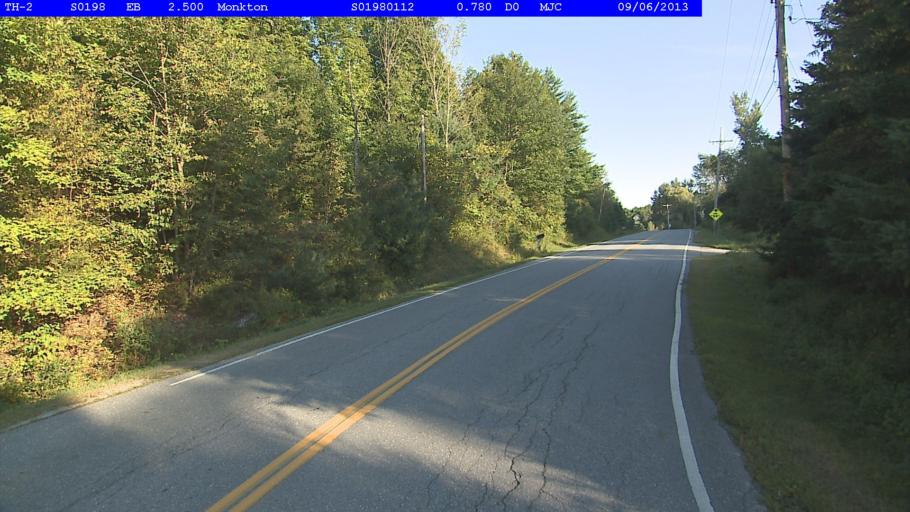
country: US
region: Vermont
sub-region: Chittenden County
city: Hinesburg
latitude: 44.2539
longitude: -73.1798
